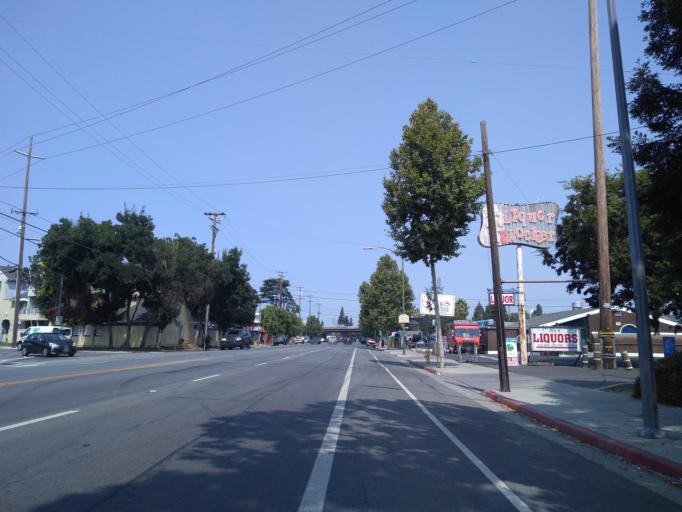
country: US
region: California
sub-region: Santa Clara County
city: Buena Vista
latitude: 37.3140
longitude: -121.9052
